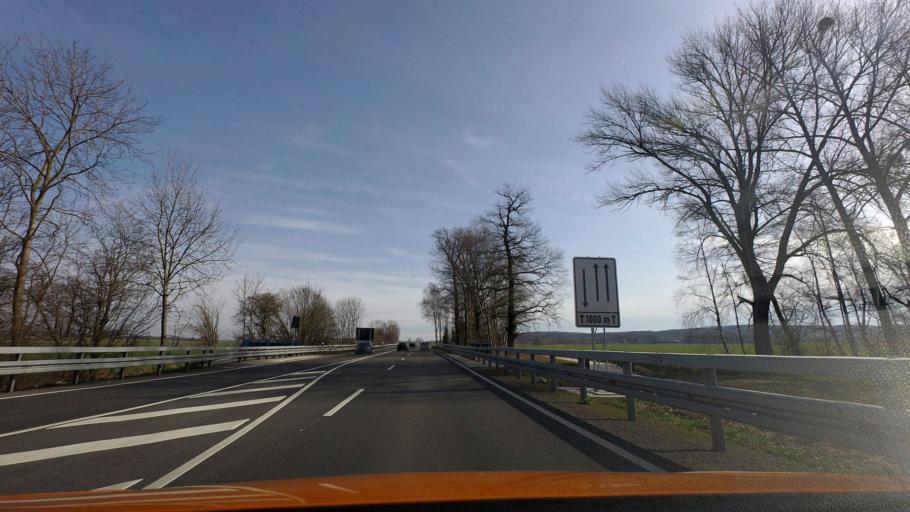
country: DE
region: Lower Saxony
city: Heuerssen
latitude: 52.3318
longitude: 9.2506
